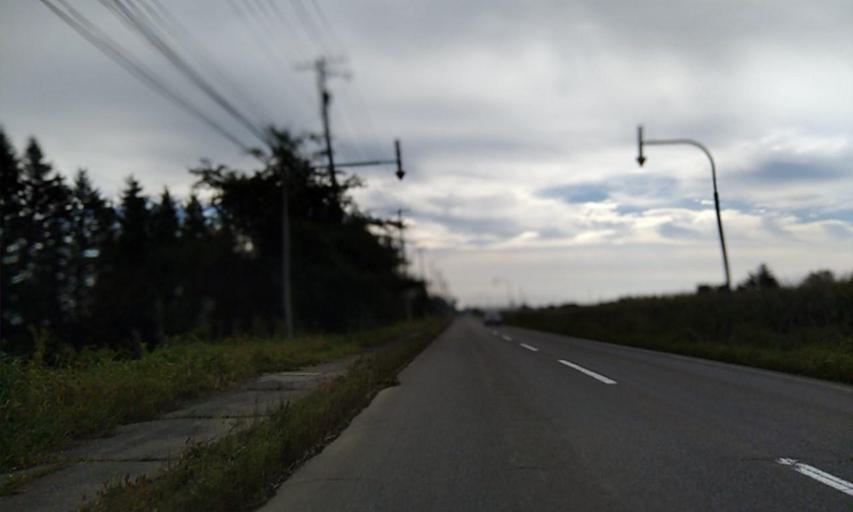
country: JP
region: Hokkaido
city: Obihiro
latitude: 42.8535
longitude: 143.1564
